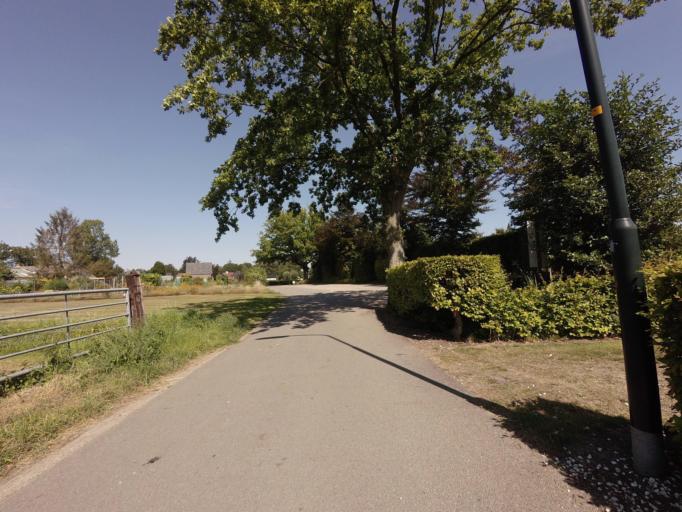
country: NL
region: Gelderland
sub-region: Gemeente Apeldoorn
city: Loenen
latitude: 52.1129
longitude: 6.0243
